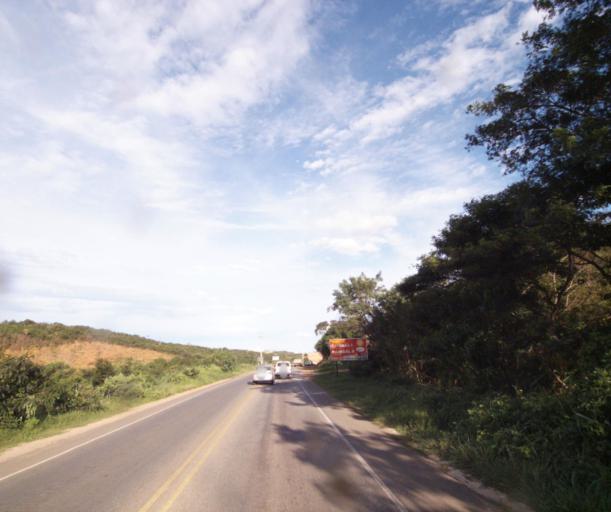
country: BR
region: Bahia
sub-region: Caetite
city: Caetite
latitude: -14.0617
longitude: -42.5030
